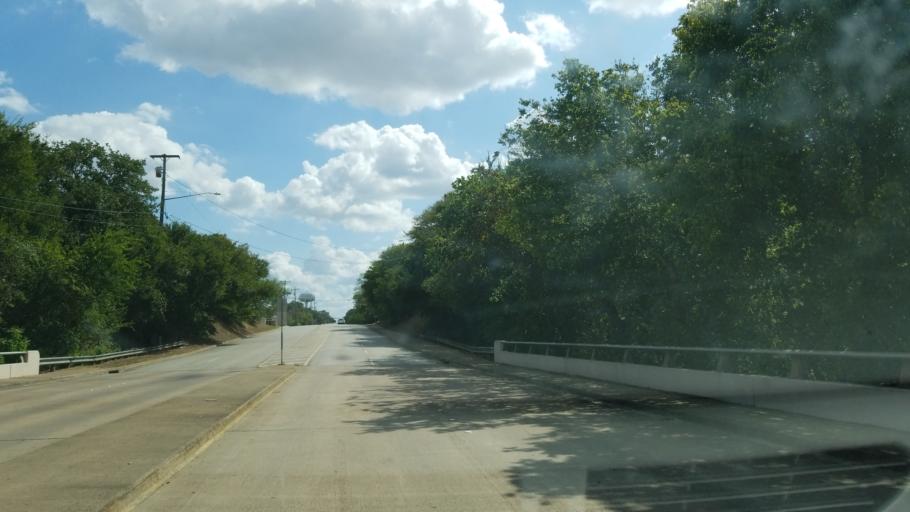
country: US
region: Texas
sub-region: Tarrant County
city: Euless
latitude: 32.8658
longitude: -97.0825
